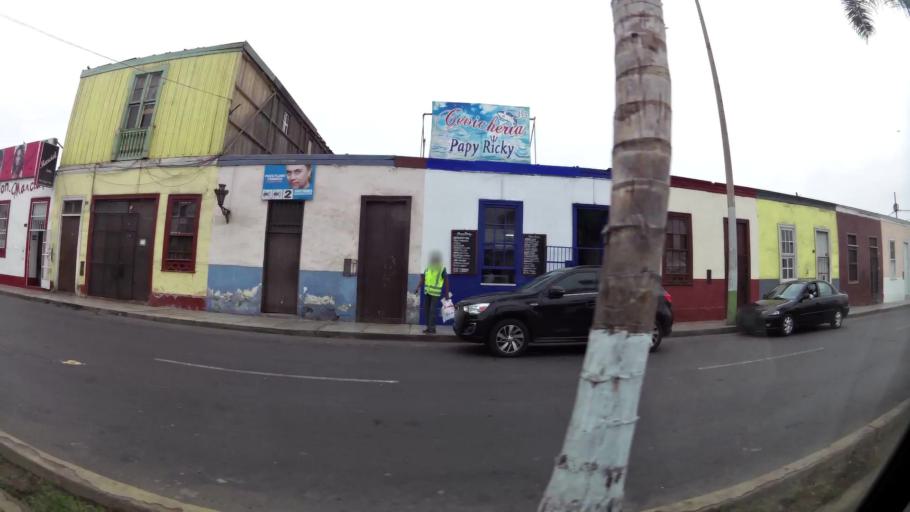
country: PE
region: Callao
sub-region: Callao
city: Callao
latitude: -12.0646
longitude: -77.1533
